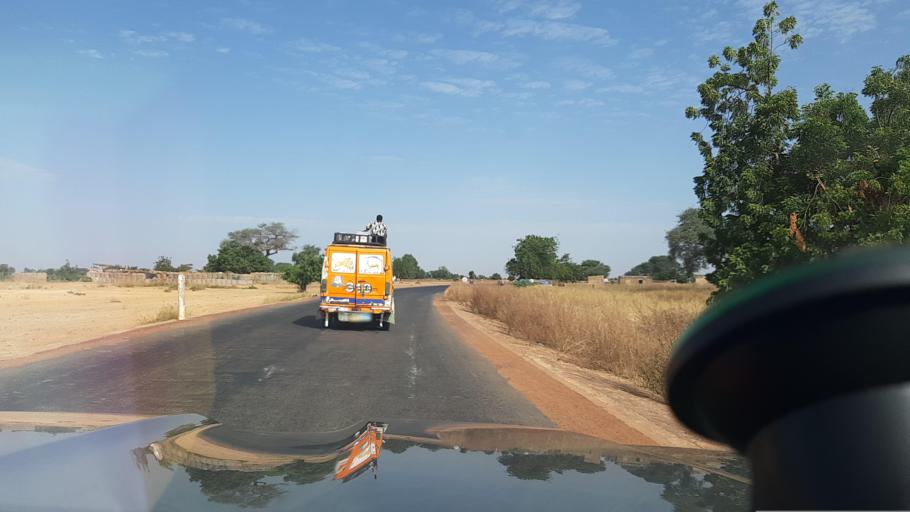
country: ML
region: Segou
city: Markala
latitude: 13.6887
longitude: -6.1003
